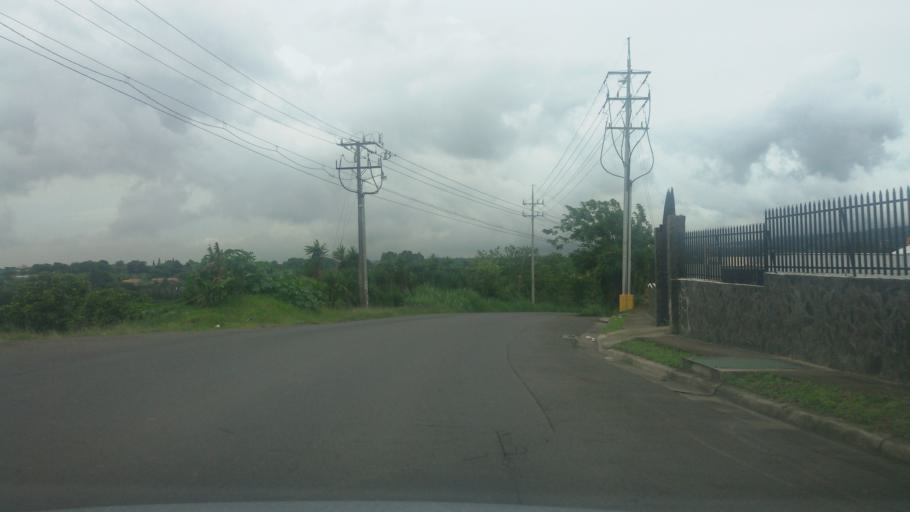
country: CR
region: Heredia
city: Angeles
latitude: 9.9807
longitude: -84.0564
